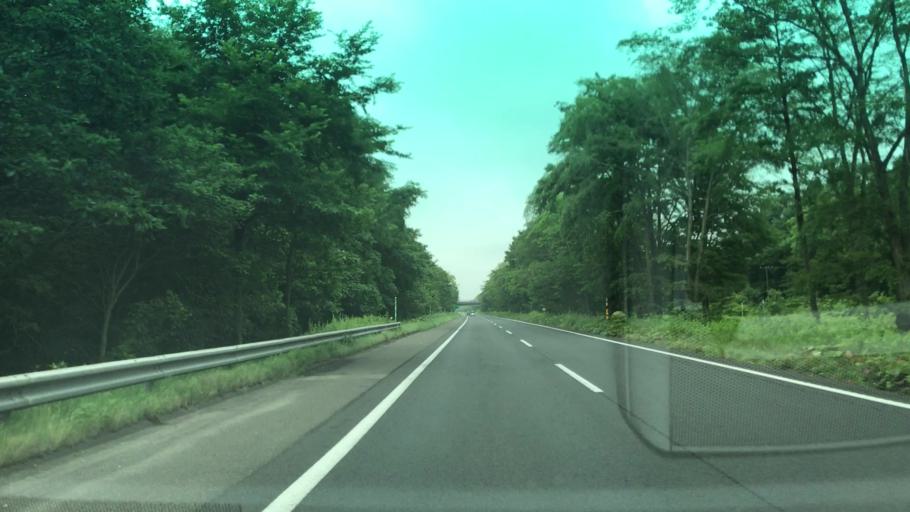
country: JP
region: Hokkaido
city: Chitose
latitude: 42.7504
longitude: 141.6460
